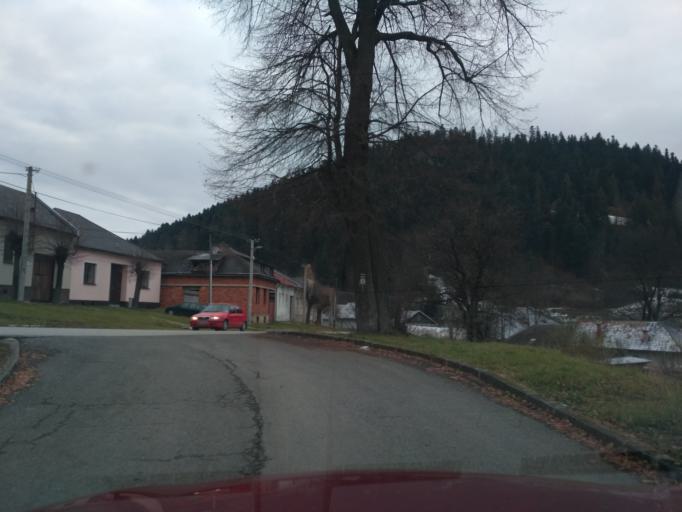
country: SK
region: Kosicky
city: Spisska Nova Ves
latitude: 48.8399
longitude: 20.6220
